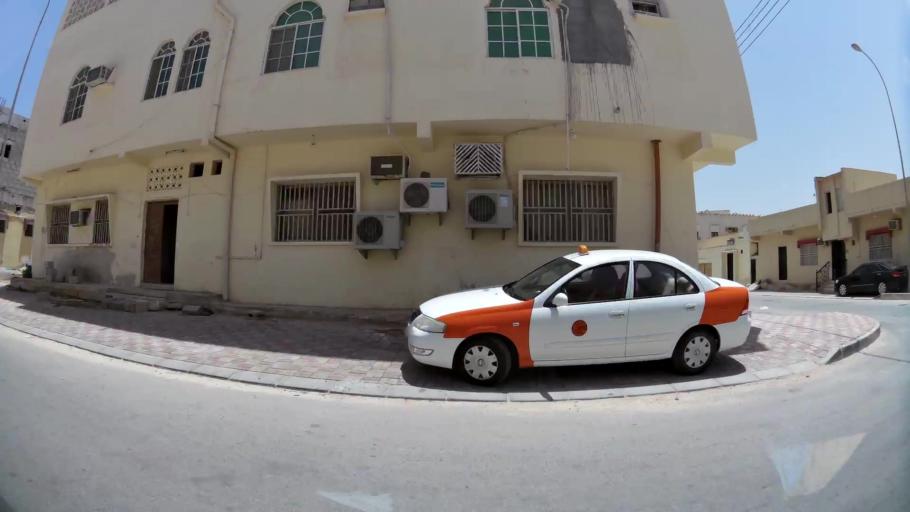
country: OM
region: Zufar
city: Salalah
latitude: 17.0183
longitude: 54.0820
